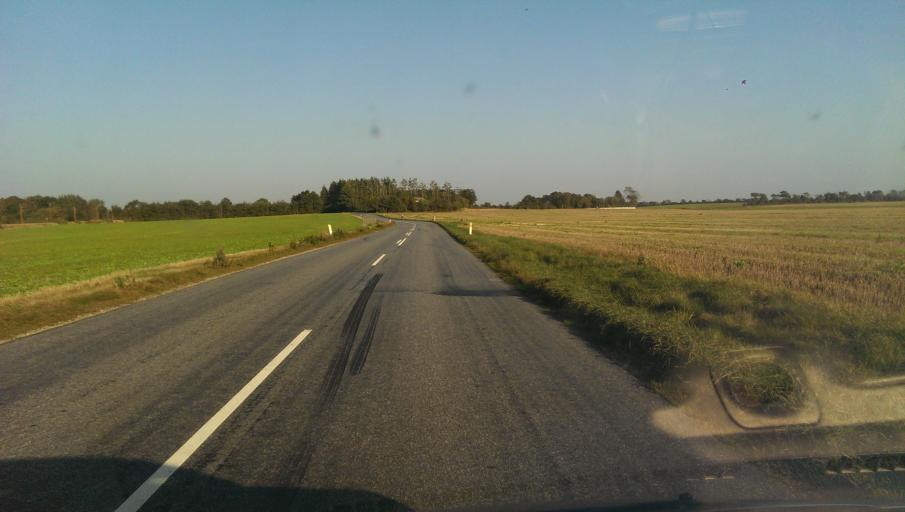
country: DK
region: South Denmark
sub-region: Esbjerg Kommune
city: Bramming
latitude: 55.4678
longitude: 8.7806
